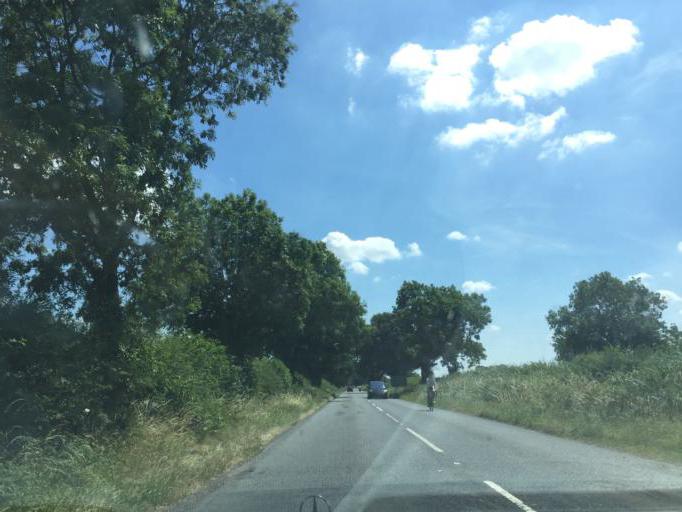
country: GB
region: England
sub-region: Leicestershire
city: Hinckley
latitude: 52.4959
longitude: -1.3571
